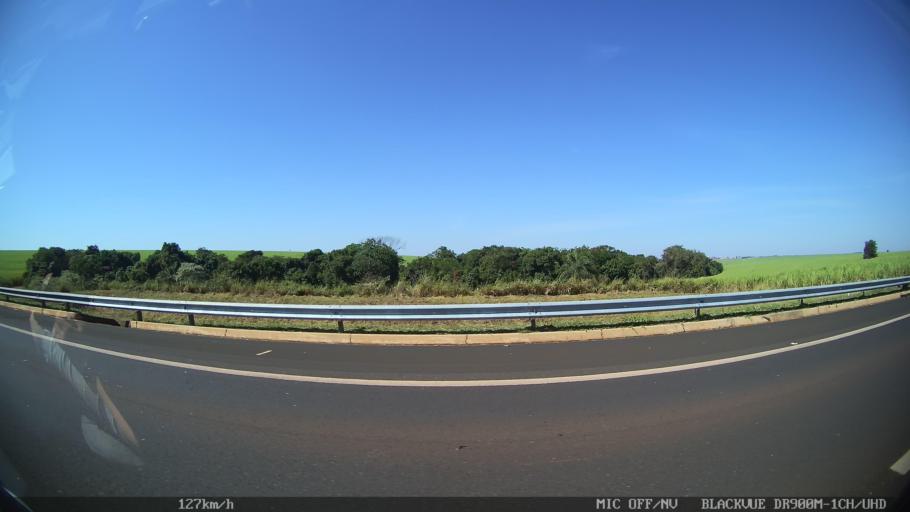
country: BR
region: Sao Paulo
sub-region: Batatais
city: Batatais
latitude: -20.8237
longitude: -47.5919
